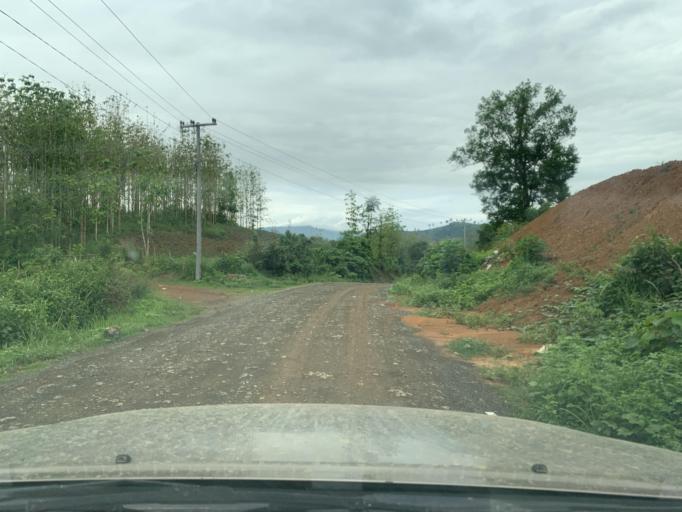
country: LA
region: Vientiane
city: Muang Sanakham
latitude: 18.4104
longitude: 101.4870
